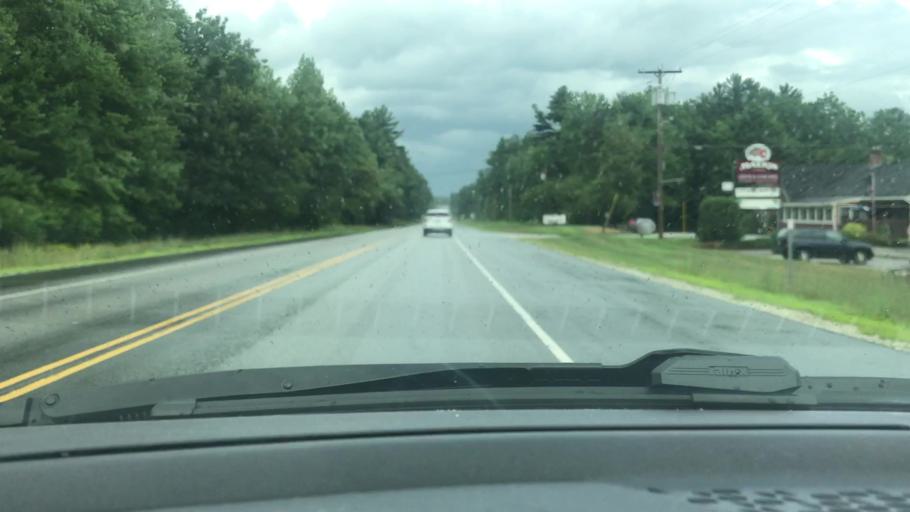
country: US
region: New Hampshire
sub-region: Merrimack County
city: Chichester
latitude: 43.2391
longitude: -71.4679
